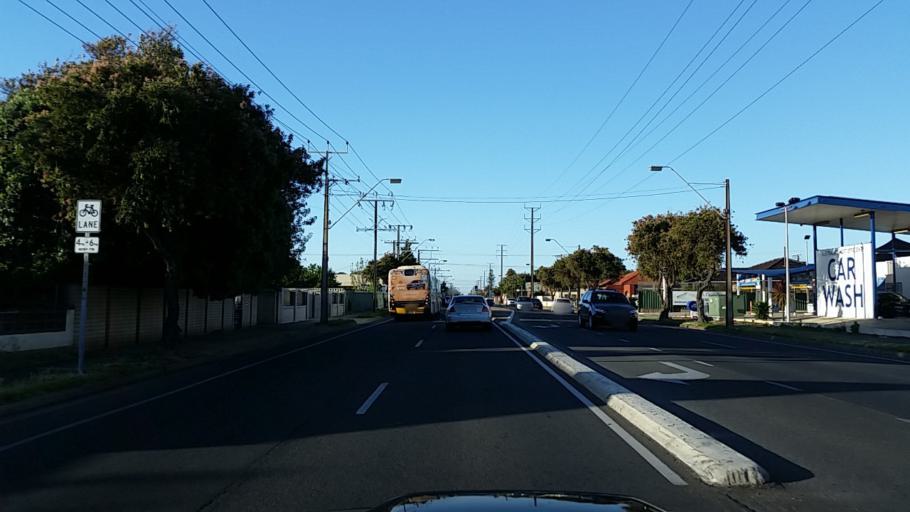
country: AU
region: South Australia
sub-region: Charles Sturt
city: Royal Park
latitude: -34.8866
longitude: 138.5133
